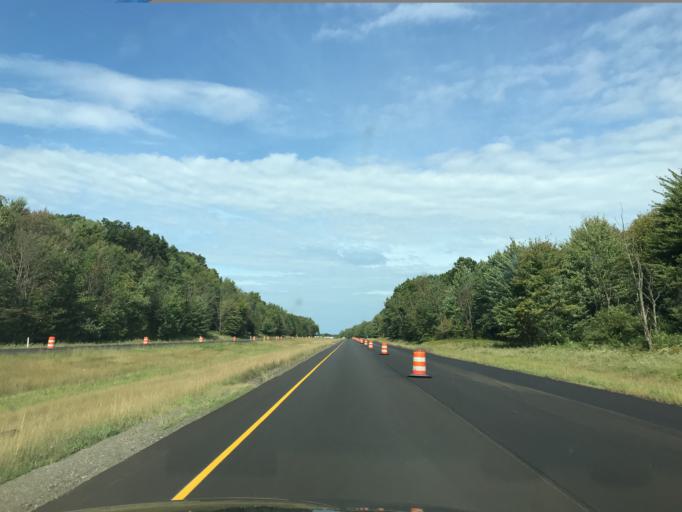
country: US
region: Ohio
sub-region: Ashtabula County
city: Jefferson
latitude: 41.7872
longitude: -80.7363
